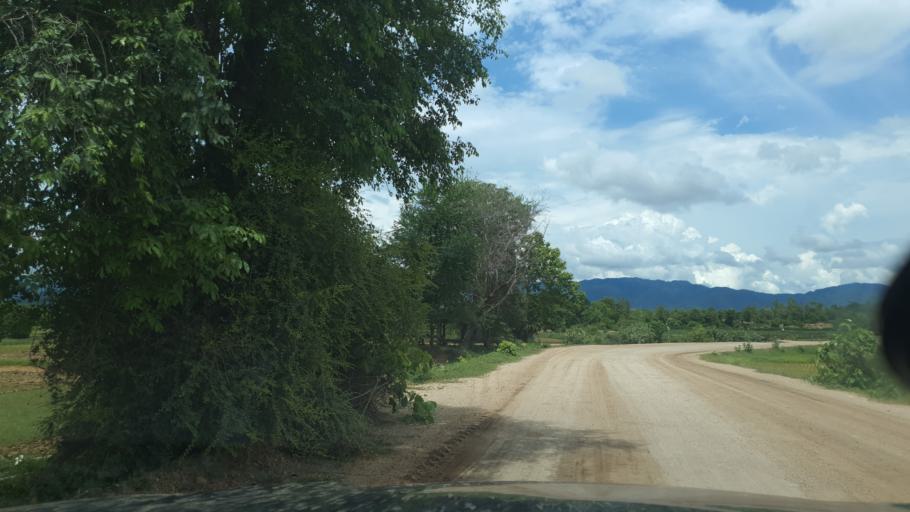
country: TH
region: Lampang
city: Sop Prap
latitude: 17.9375
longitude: 99.3619
